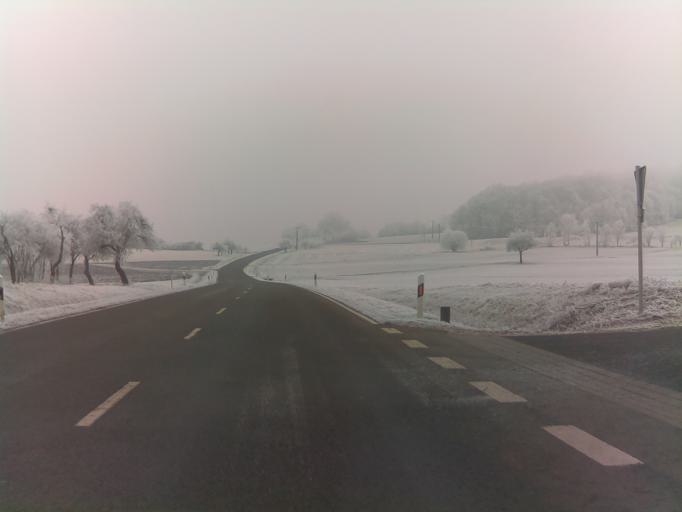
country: DE
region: Bavaria
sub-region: Regierungsbezirk Unterfranken
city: Oberelsbach
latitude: 50.4558
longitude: 10.1338
